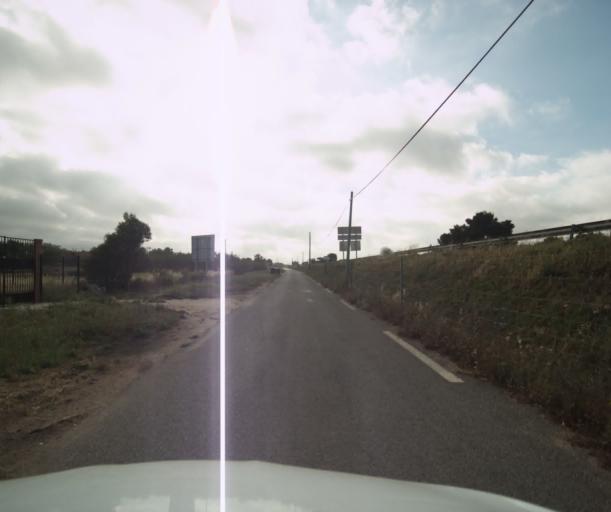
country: FR
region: Provence-Alpes-Cote d'Azur
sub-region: Departement du Var
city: Ollioules
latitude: 43.1211
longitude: 5.8378
